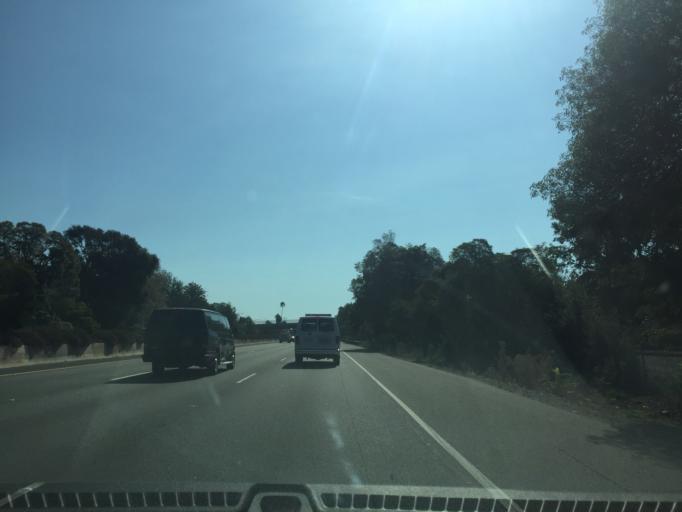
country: US
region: California
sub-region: Santa Barbara County
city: Santa Barbara
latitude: 34.4229
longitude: -119.7169
